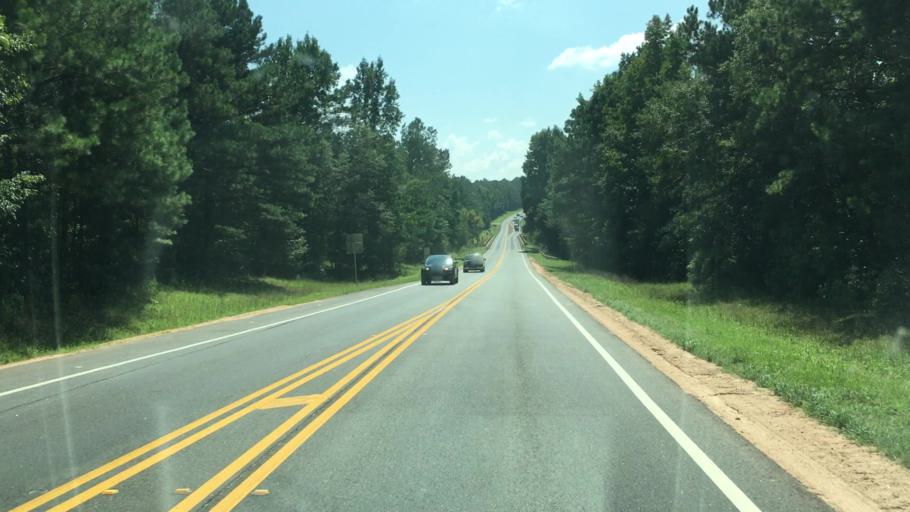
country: US
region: Georgia
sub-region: Morgan County
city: Madison
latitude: 33.7209
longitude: -83.4327
